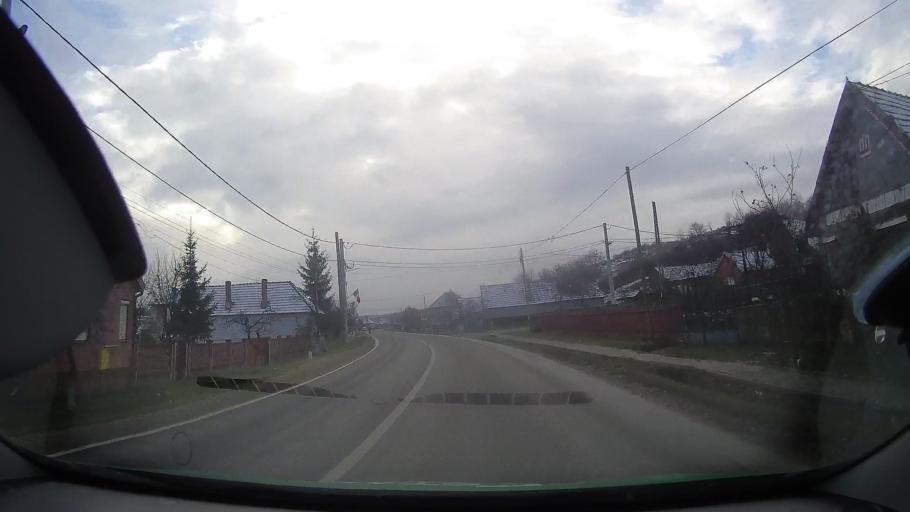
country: RO
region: Mures
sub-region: Comuna Cucerdea
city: Cucerdea
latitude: 46.4060
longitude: 24.2651
